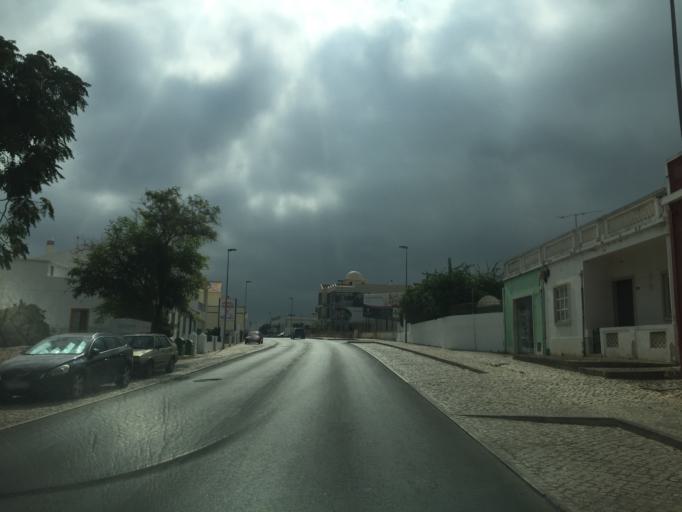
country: PT
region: Faro
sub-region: Loule
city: Almancil
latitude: 37.0856
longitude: -8.0280
